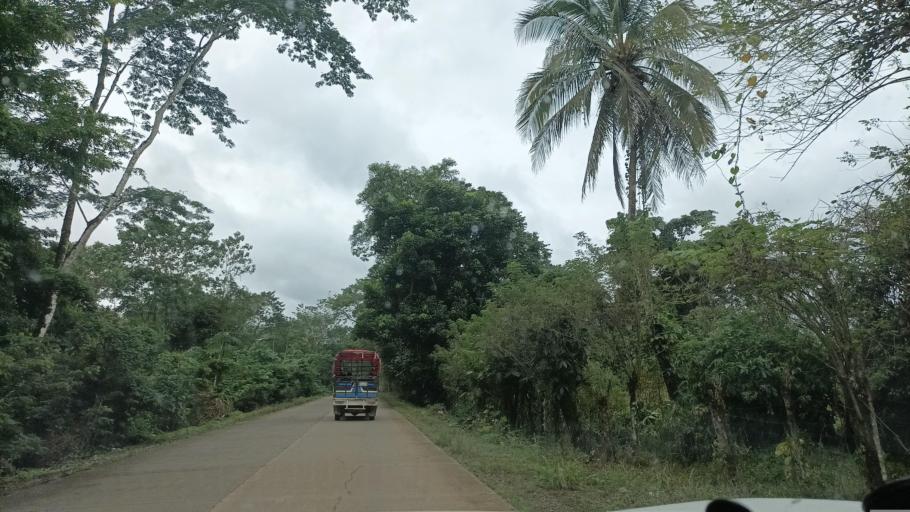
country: MX
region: Veracruz
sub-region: Uxpanapa
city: Poblado 10
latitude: 17.2787
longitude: -94.4805
